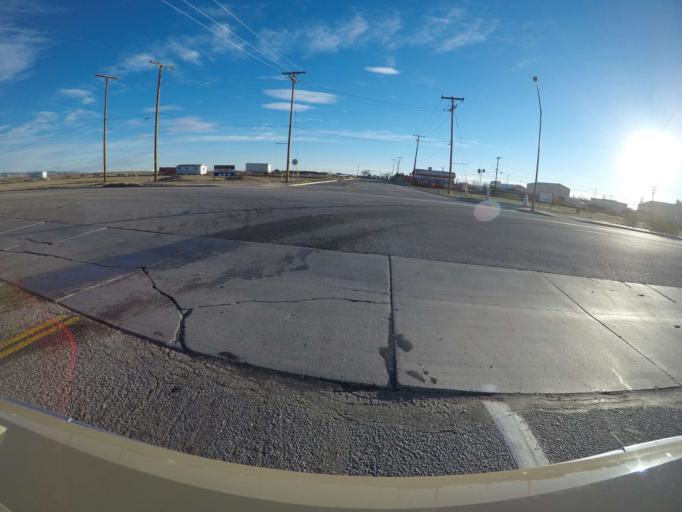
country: US
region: California
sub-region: Kern County
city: Mojave
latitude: 35.0577
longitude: -118.1742
